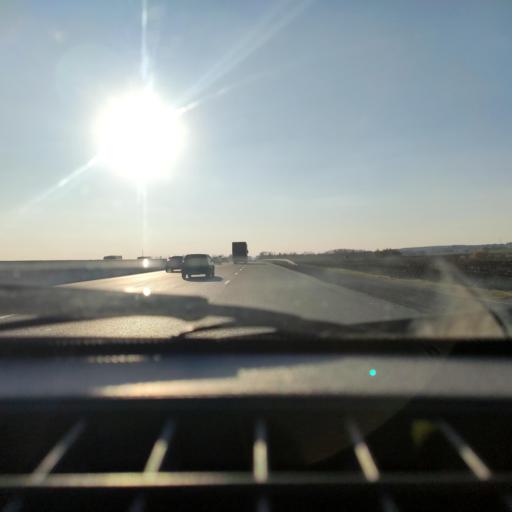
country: RU
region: Bashkortostan
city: Avdon
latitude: 54.6731
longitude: 55.7759
